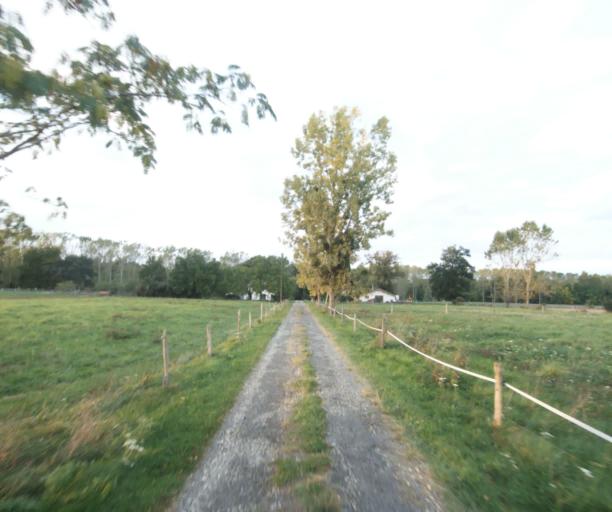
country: FR
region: Aquitaine
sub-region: Departement des Landes
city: Gabarret
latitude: 43.9687
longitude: 0.1056
